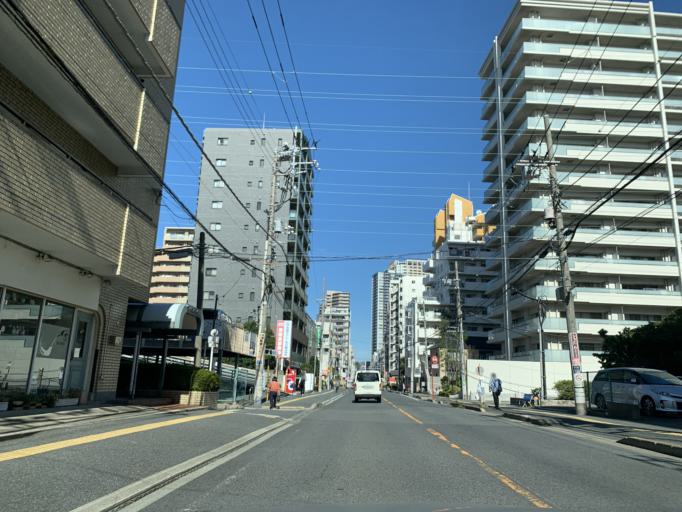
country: JP
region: Tokyo
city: Urayasu
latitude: 35.7183
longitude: 139.9233
